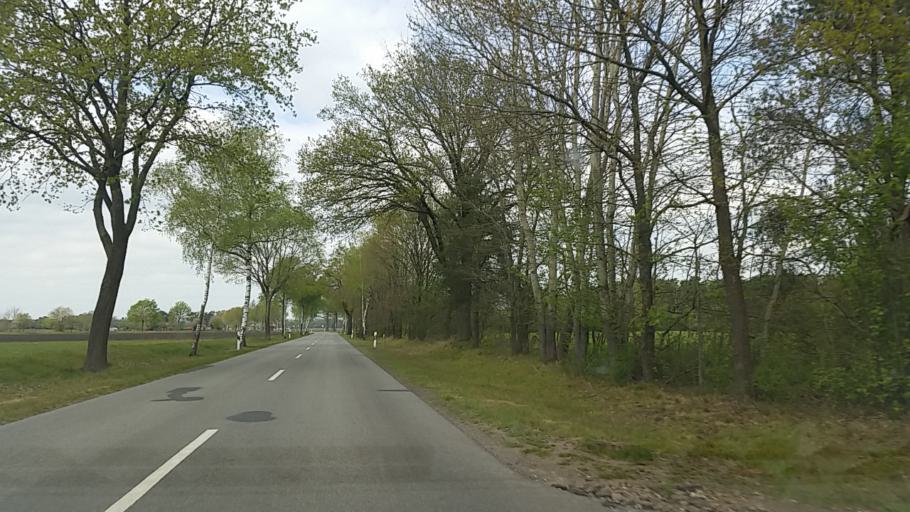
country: DE
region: Lower Saxony
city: Otter
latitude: 53.1921
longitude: 9.7306
